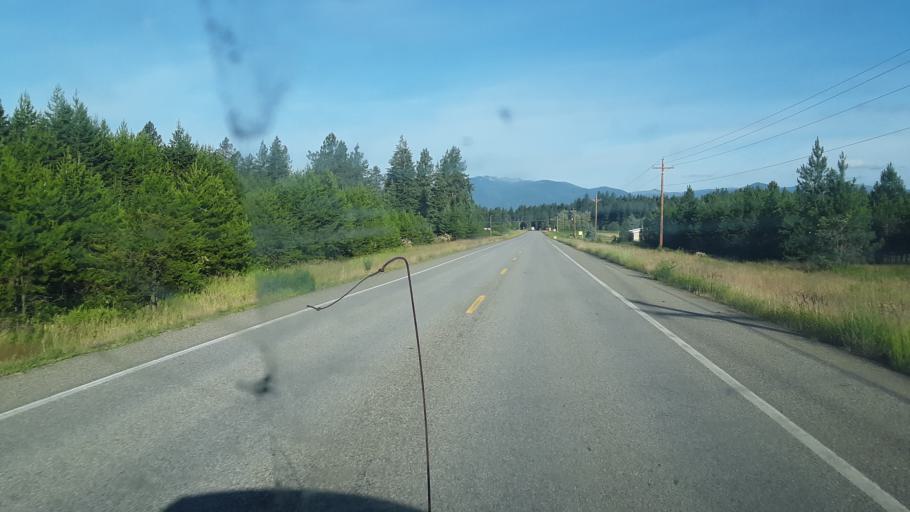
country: US
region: Idaho
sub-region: Boundary County
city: Bonners Ferry
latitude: 48.7298
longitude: -116.2336
